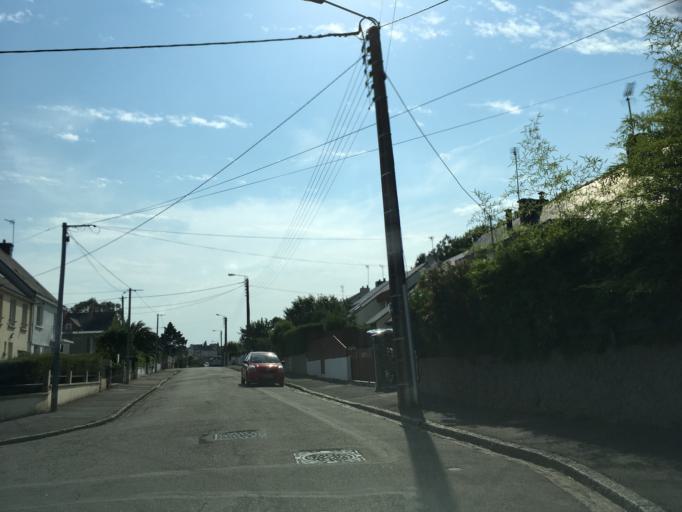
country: FR
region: Brittany
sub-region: Departement du Morbihan
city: Lorient
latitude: 47.7633
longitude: -3.3706
